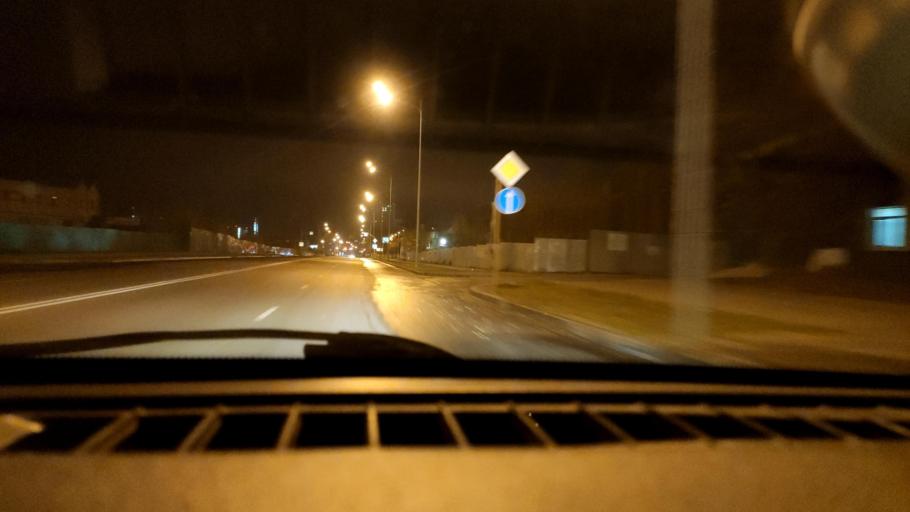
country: RU
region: Samara
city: Samara
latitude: 53.2058
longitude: 50.1567
